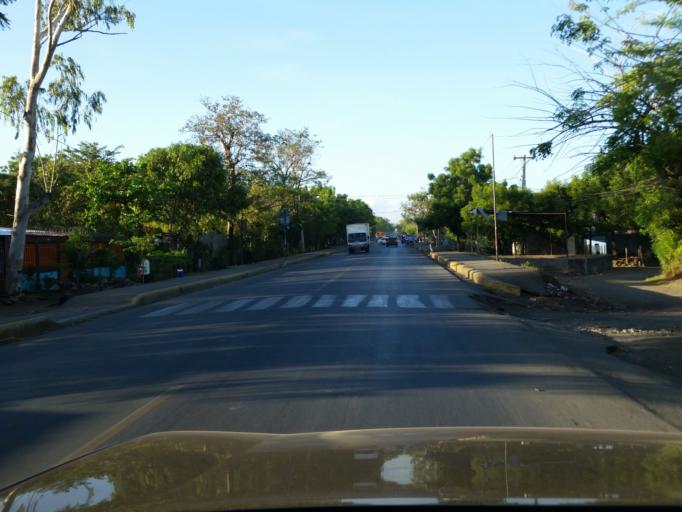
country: NI
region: Managua
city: Tipitapa
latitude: 12.1866
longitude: -86.0966
